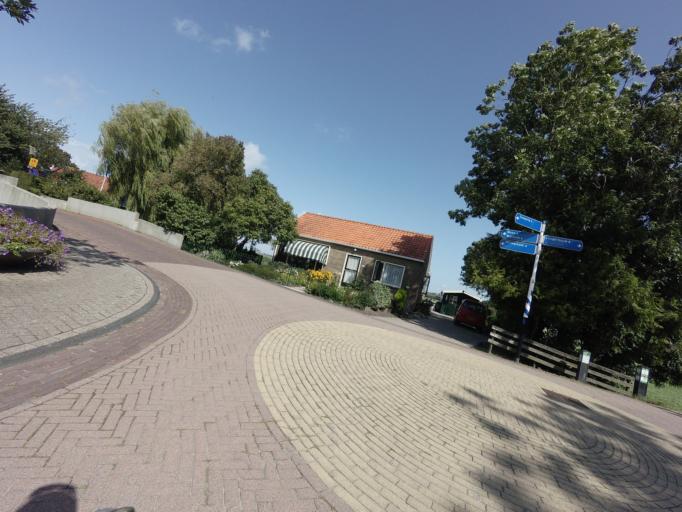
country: NL
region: Friesland
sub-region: Sudwest Fryslan
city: Makkum
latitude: 53.0807
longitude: 5.4529
